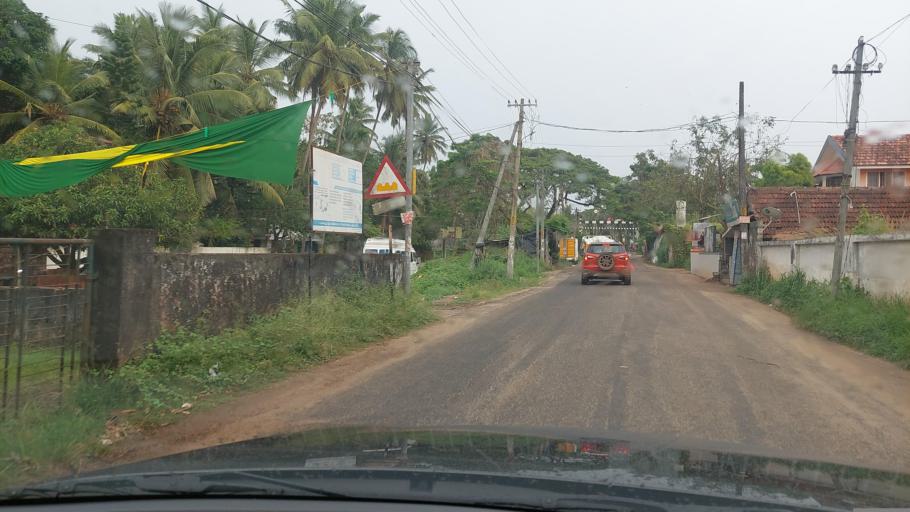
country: IN
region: Kerala
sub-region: Kozhikode
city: Kozhikode
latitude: 11.2917
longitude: 75.7615
